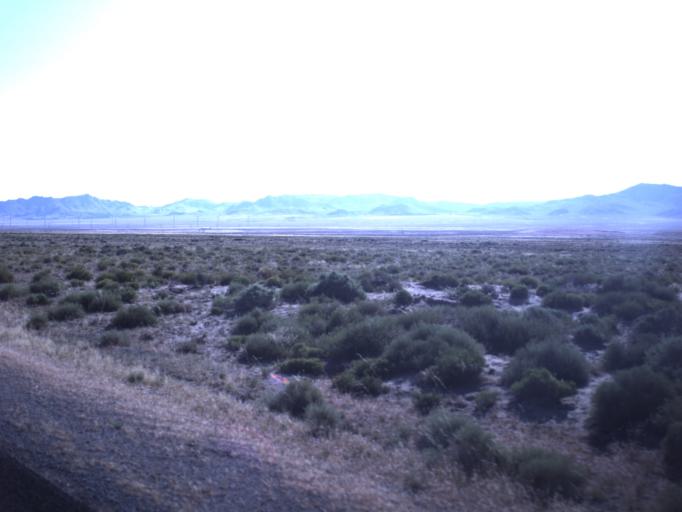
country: US
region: Utah
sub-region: Beaver County
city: Milford
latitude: 38.4640
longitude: -113.0009
